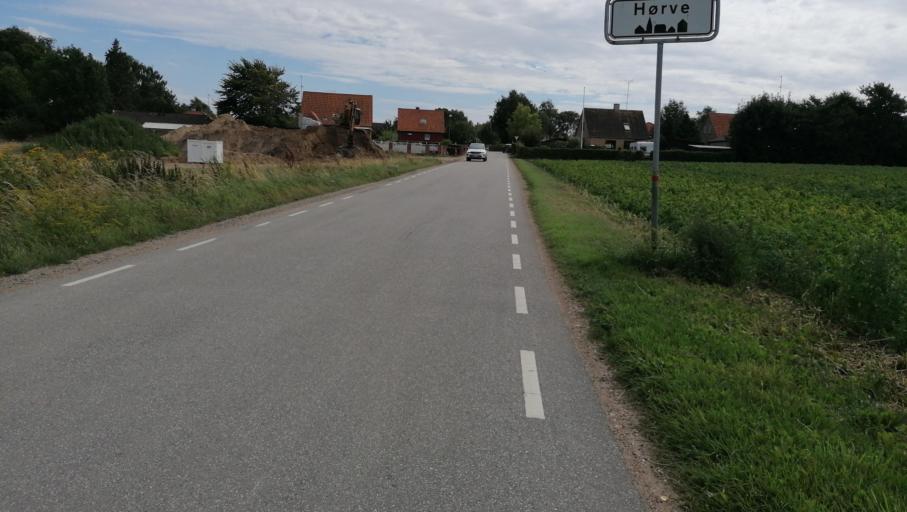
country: DK
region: Zealand
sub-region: Odsherred Kommune
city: Horve
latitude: 55.7526
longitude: 11.4410
